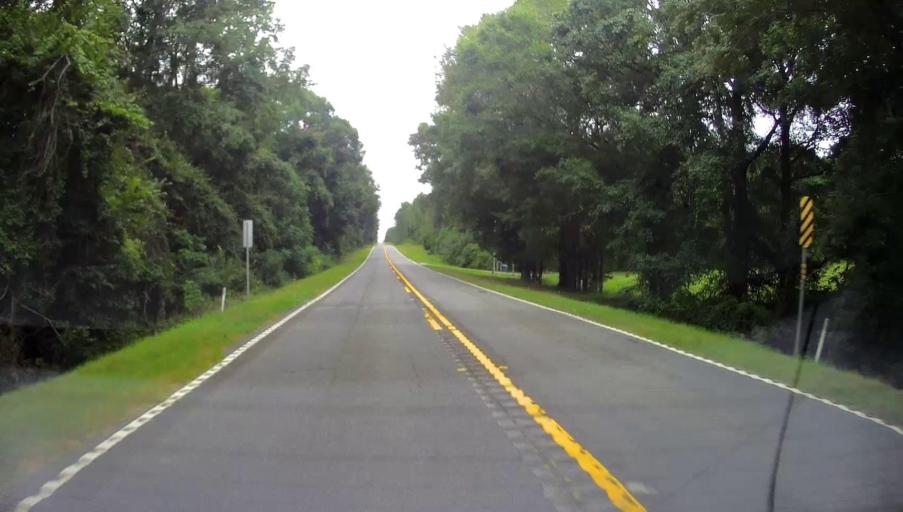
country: US
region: Georgia
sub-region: Dooly County
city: Unadilla
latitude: 32.2912
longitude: -83.8654
